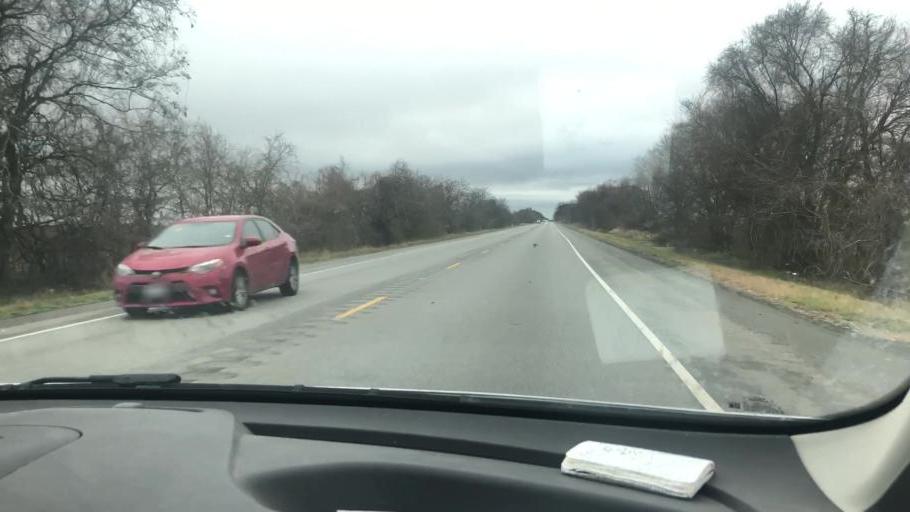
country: US
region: Texas
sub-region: Matagorda County
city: Bay City
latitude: 29.1158
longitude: -95.9800
